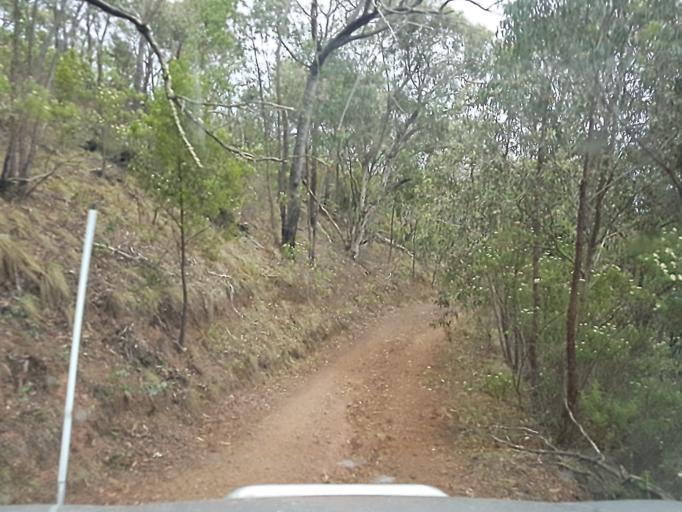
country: AU
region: New South Wales
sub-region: Snowy River
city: Jindabyne
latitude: -36.9229
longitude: 148.3427
